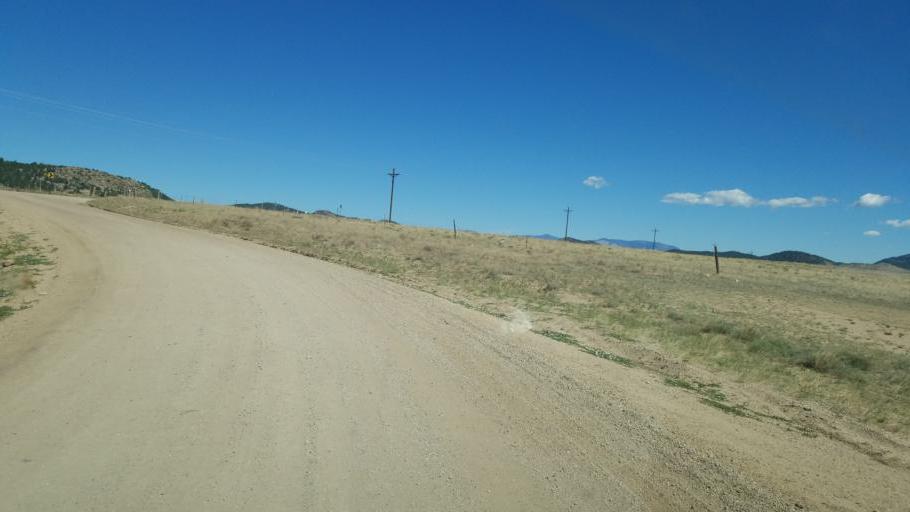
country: US
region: Colorado
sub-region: Custer County
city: Westcliffe
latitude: 38.2623
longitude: -105.5002
